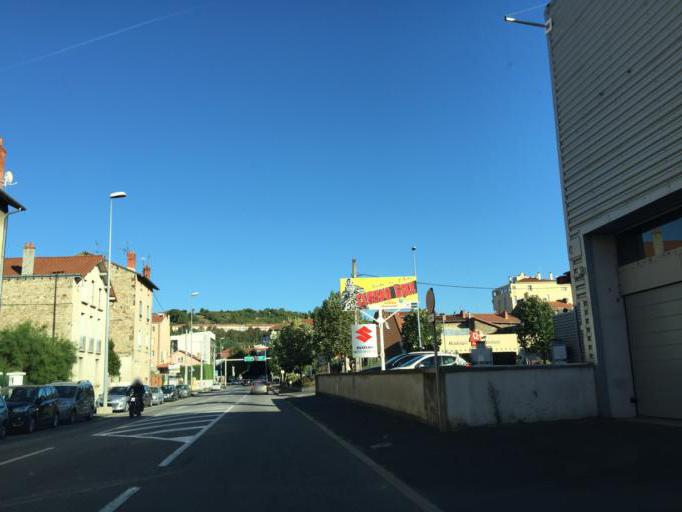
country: FR
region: Auvergne
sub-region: Departement de la Haute-Loire
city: Le Puy-en-Velay
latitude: 45.0489
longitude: 3.8916
